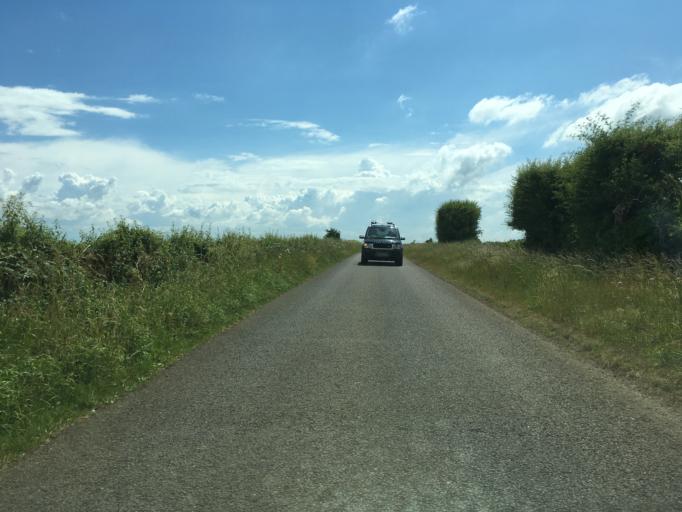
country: GB
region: England
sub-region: Gloucestershire
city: Coates
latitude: 51.7144
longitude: -2.0906
